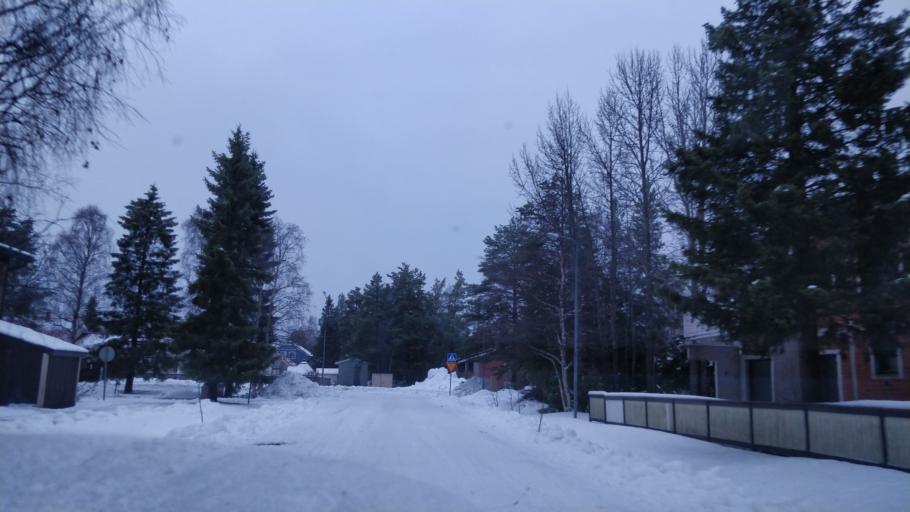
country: FI
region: Lapland
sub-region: Kemi-Tornio
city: Kemi
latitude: 65.7426
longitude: 24.6011
